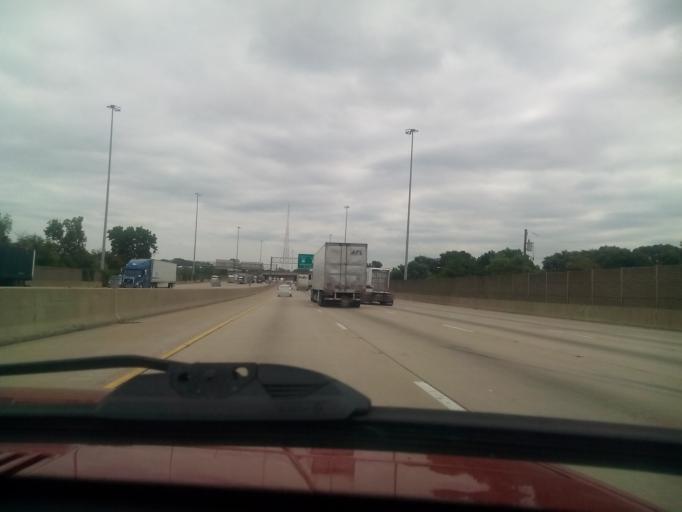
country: US
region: Illinois
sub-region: Cook County
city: Lansing
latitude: 41.5777
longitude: -87.5362
